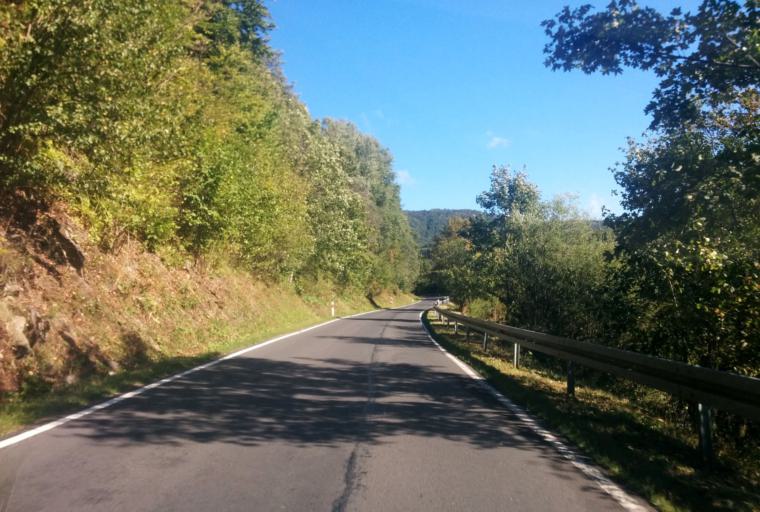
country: PL
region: Subcarpathian Voivodeship
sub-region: Powiat bieszczadzki
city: Lutowiska
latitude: 49.1200
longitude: 22.6652
